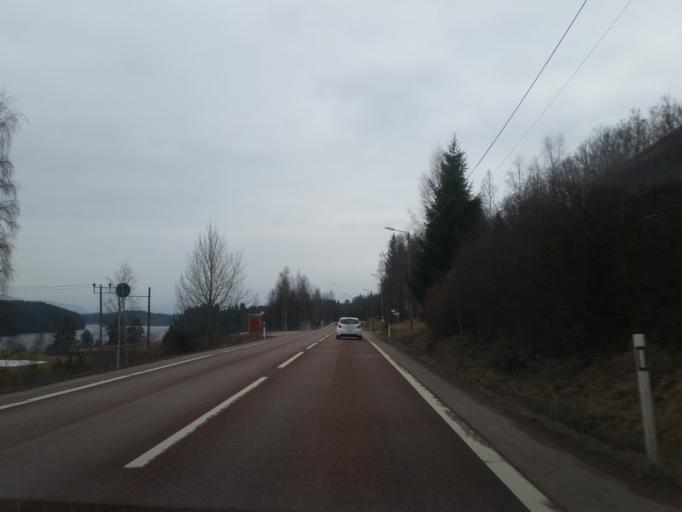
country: SE
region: Dalarna
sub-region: Alvdalens Kommun
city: AElvdalen
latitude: 61.1910
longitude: 14.0853
